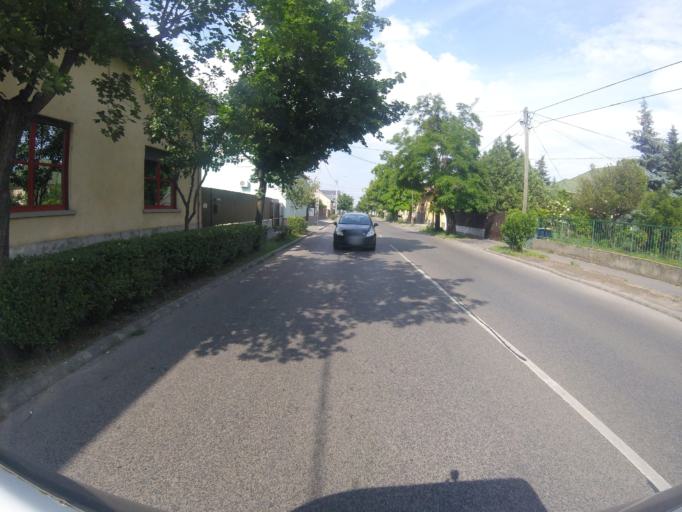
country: HU
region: Budapest
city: Budapest XX. keruelet
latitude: 47.4408
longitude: 19.1185
